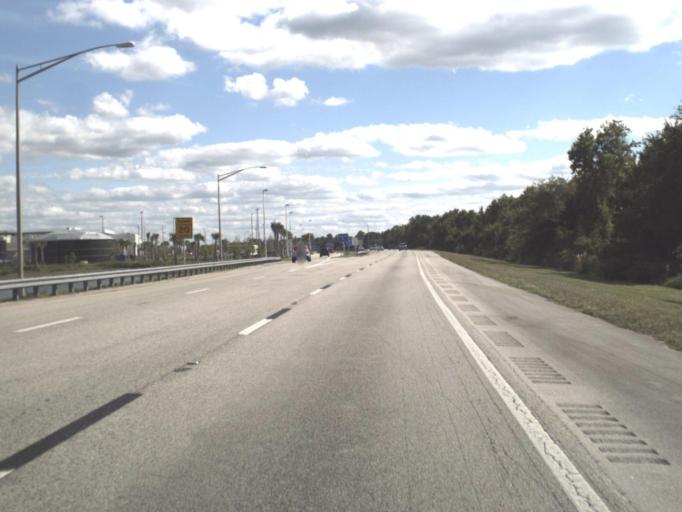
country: US
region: Florida
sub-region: Indian River County
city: Fellsmere
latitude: 27.6047
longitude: -80.8256
